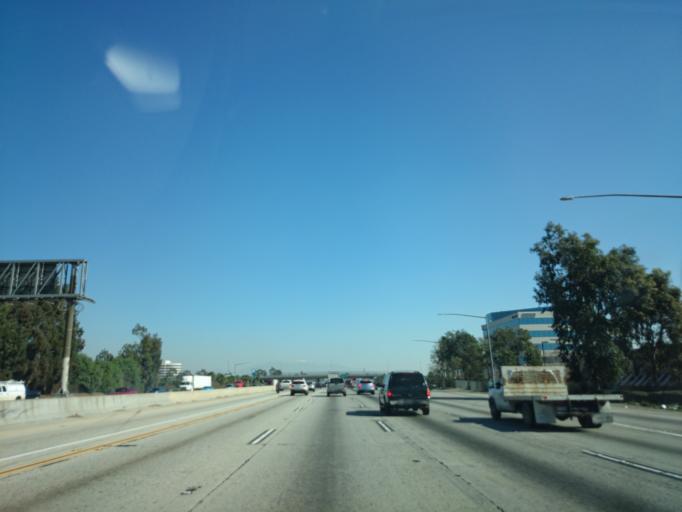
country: US
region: California
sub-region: San Bernardino County
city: Rancho Cucamonga
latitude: 34.0674
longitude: -117.5802
